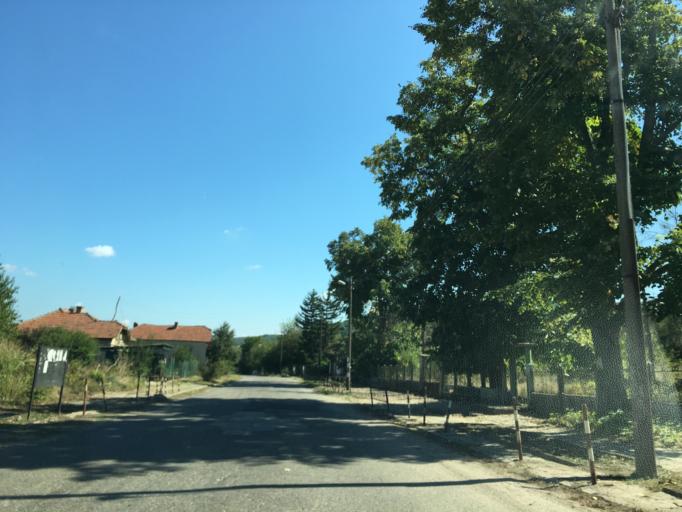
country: RO
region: Dolj
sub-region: Comuna Desa
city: Desa
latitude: 43.7647
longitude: 23.0375
